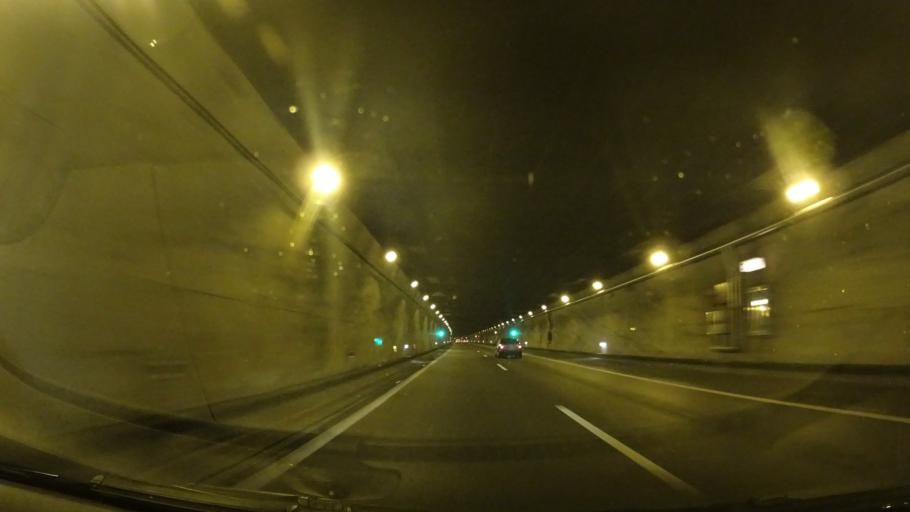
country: ES
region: Madrid
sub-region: Provincia de Madrid
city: Guadarrama
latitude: 40.7156
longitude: -4.1515
